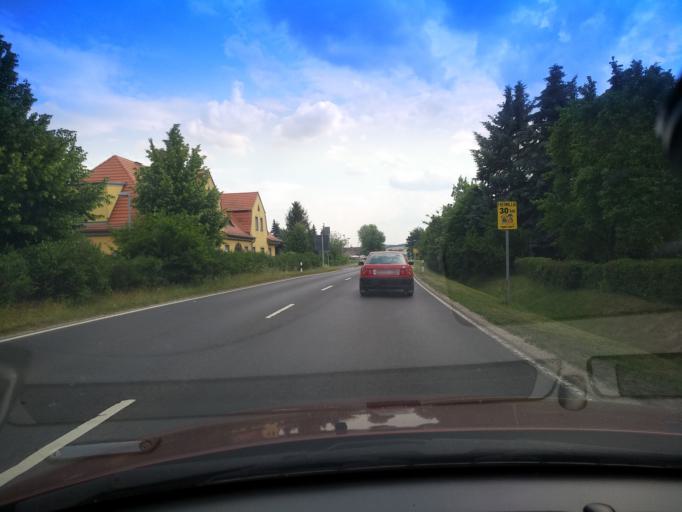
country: DE
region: Saxony
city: Kodersdorf
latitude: 51.2457
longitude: 14.8890
